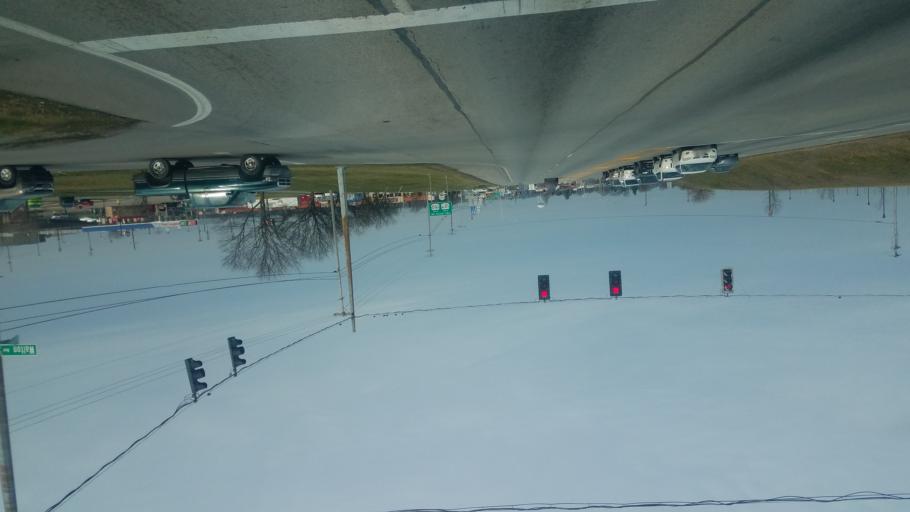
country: US
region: Kentucky
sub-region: Boyle County
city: Danville
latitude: 37.6145
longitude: -84.7744
